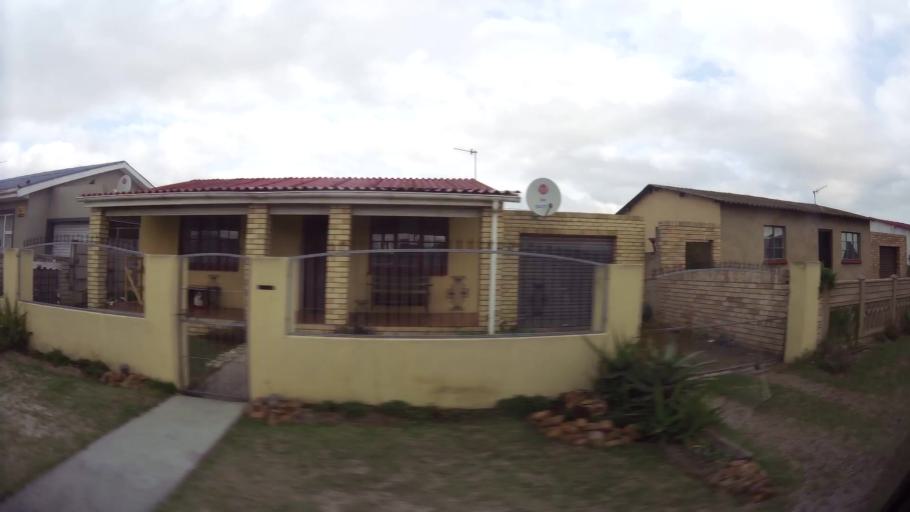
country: ZA
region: Eastern Cape
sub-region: Nelson Mandela Bay Metropolitan Municipality
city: Port Elizabeth
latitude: -33.9175
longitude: 25.5567
